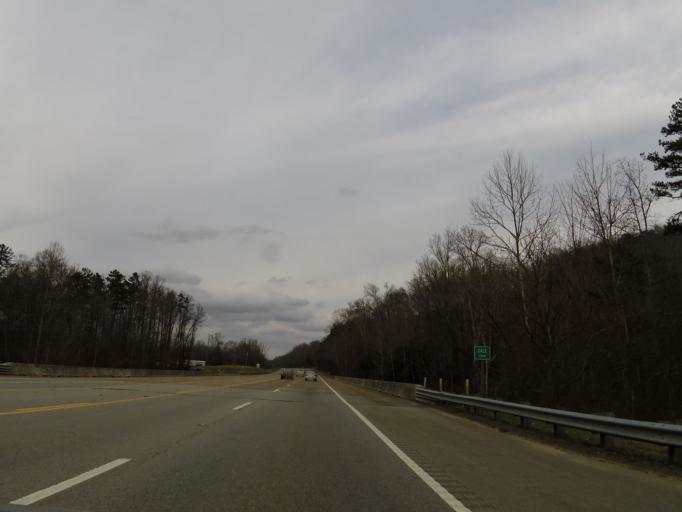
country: US
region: Tennessee
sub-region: Hamilton County
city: Sale Creek
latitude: 35.3993
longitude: -85.1043
